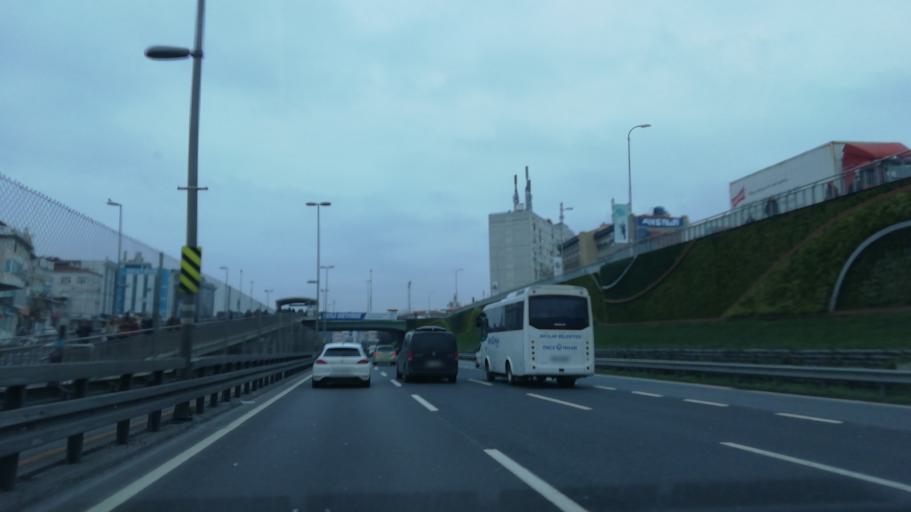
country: TR
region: Istanbul
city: Sisli
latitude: 41.0622
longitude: 28.9677
